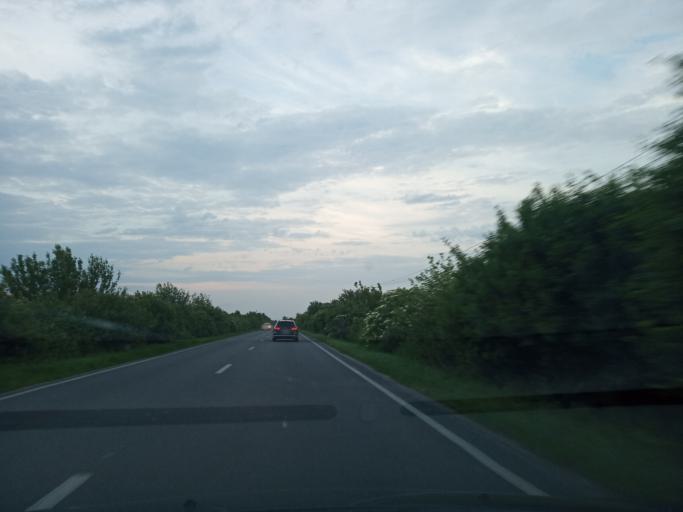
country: RO
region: Timis
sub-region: Oras Deta
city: Deta
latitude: 45.4245
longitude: 21.2299
